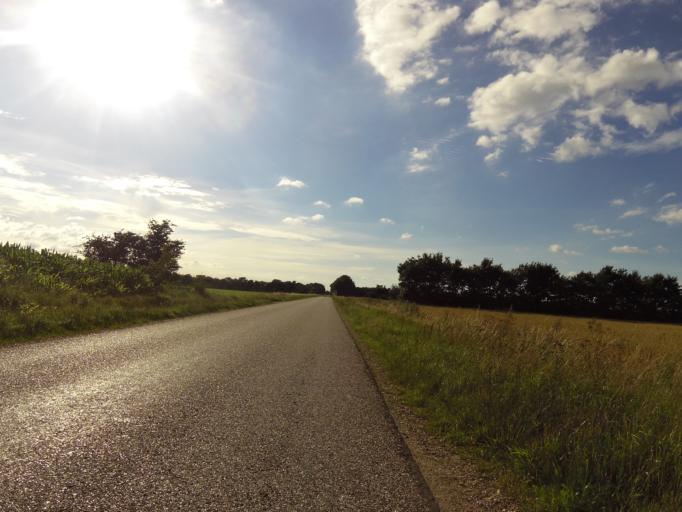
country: DK
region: South Denmark
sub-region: Haderslev Kommune
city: Vojens
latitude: 55.2028
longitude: 9.2845
